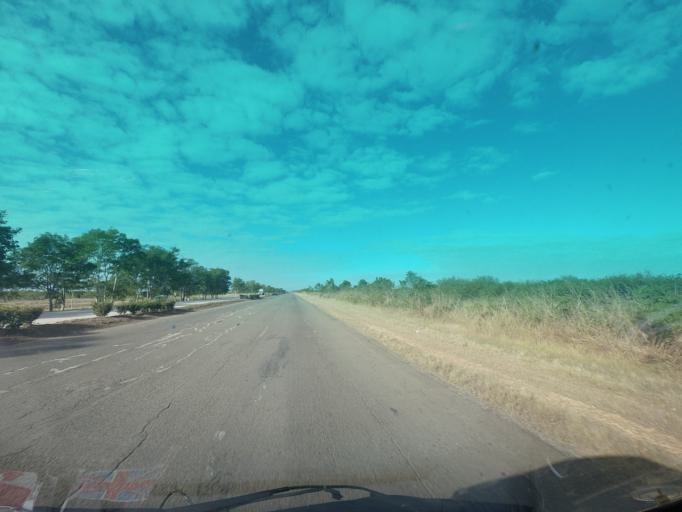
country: CU
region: Cienfuegos
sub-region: Municipio de Aguada de Pasajeros
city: Aguada de Pasajeros
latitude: 22.4313
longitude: -80.7755
